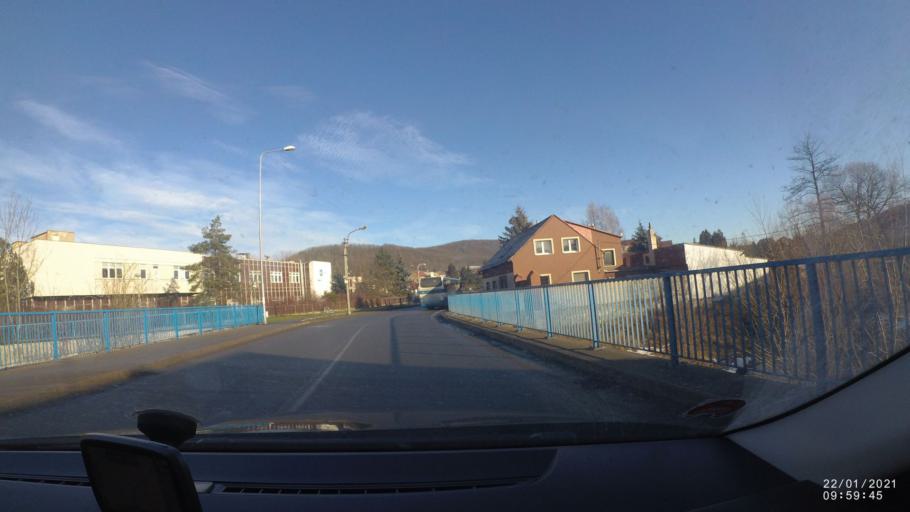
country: CZ
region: Central Bohemia
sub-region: Okres Beroun
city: Lodenice
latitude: 49.9962
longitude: 14.1589
